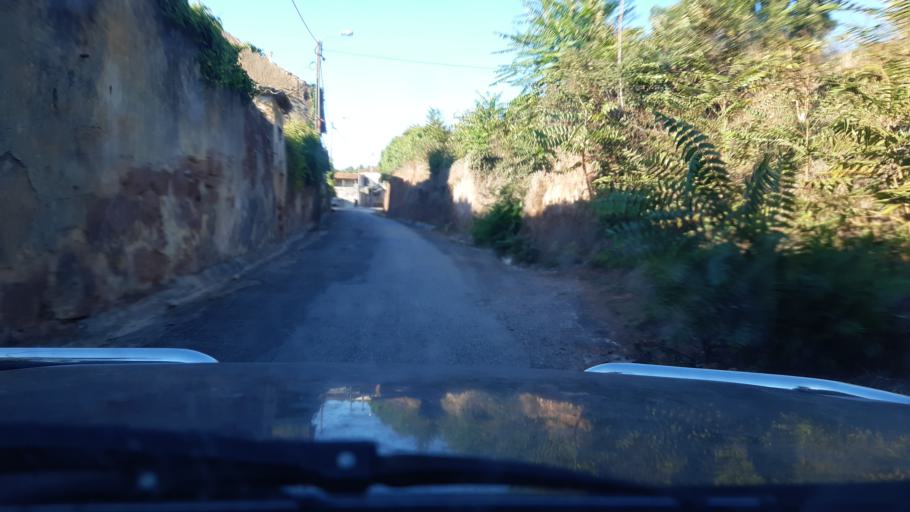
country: PT
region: Aveiro
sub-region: Agueda
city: Agueda
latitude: 40.5759
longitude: -8.4657
